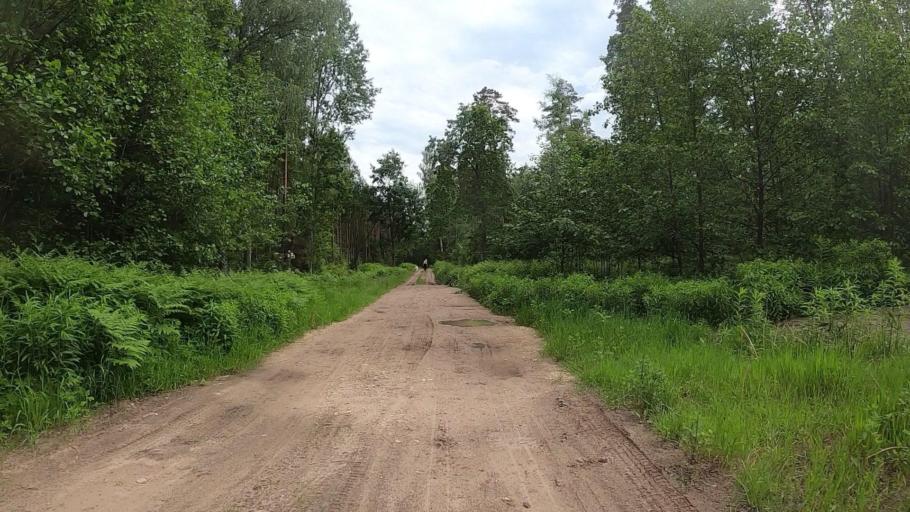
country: LV
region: Olaine
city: Olaine
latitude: 56.7475
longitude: 23.8703
